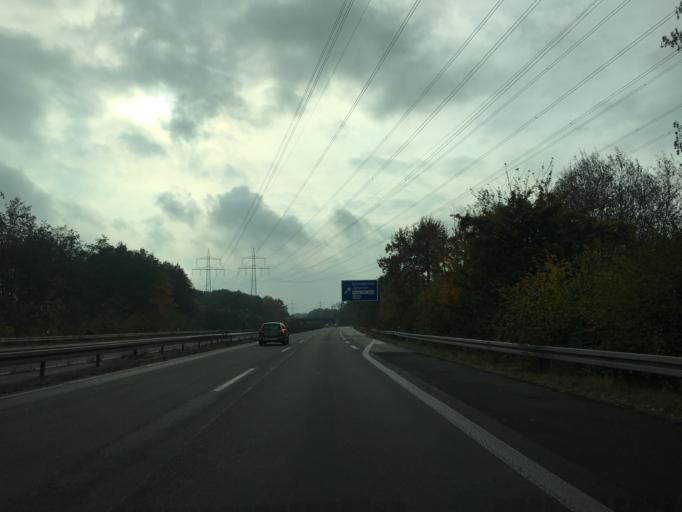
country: DE
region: North Rhine-Westphalia
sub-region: Regierungsbezirk Munster
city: Gladbeck
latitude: 51.5916
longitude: 7.0337
